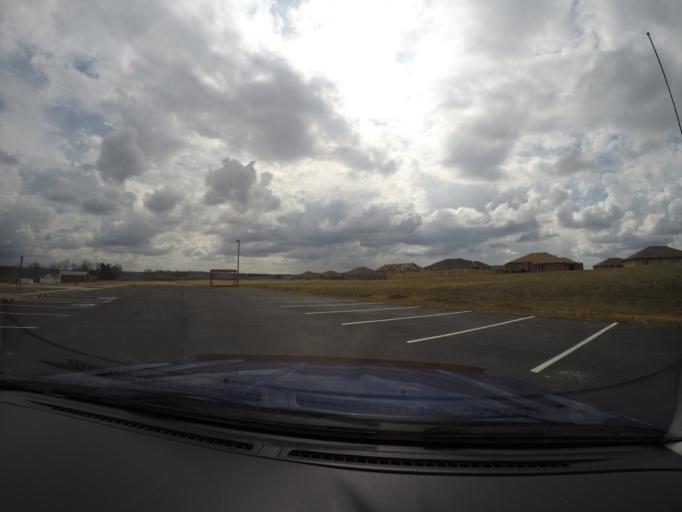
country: US
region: Kansas
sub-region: Riley County
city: Manhattan
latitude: 39.2147
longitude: -96.5120
